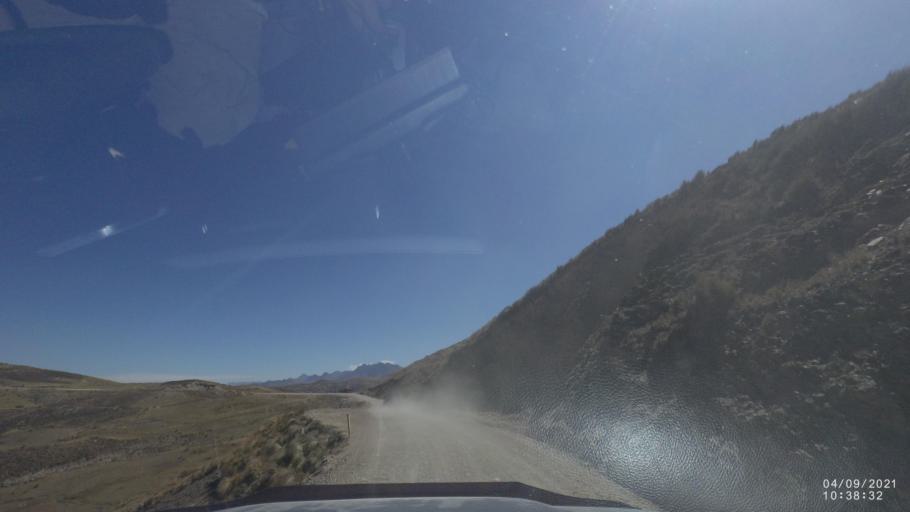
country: BO
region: Cochabamba
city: Sipe Sipe
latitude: -17.2864
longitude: -66.4579
